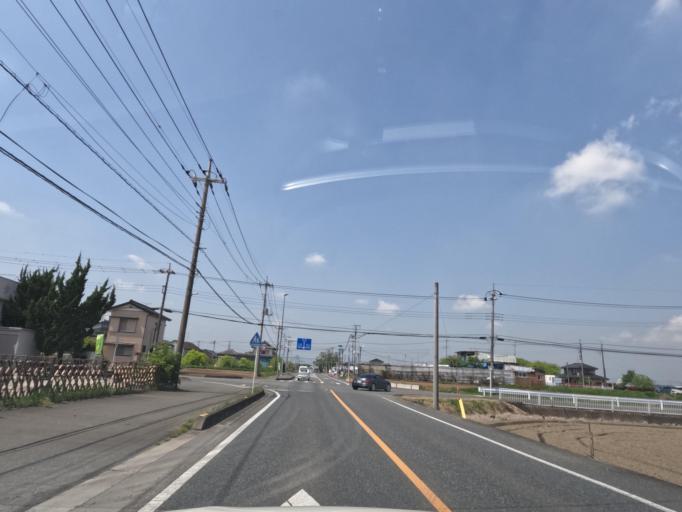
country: JP
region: Saitama
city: Kawagoe
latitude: 35.9640
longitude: 139.4943
